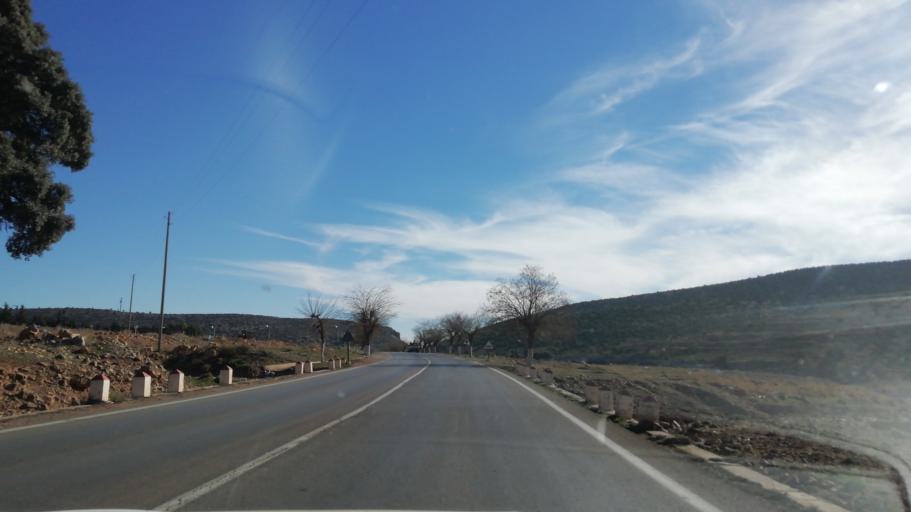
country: DZ
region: Tlemcen
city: Sebdou
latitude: 34.7080
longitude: -1.3200
